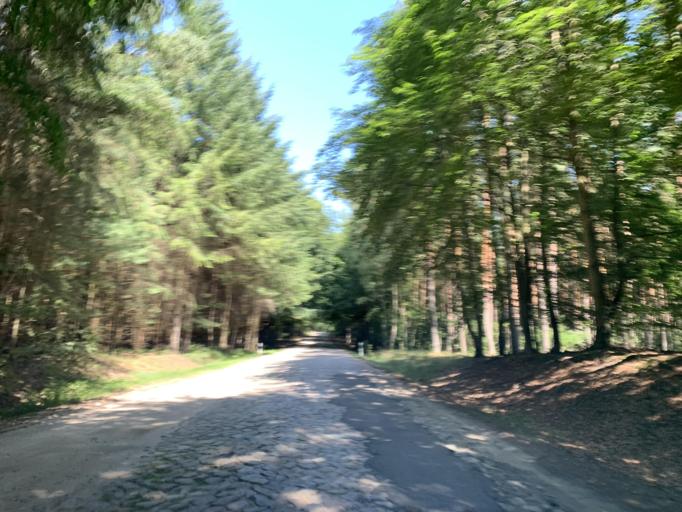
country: DE
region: Mecklenburg-Vorpommern
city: Carpin
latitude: 53.3153
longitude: 13.2647
